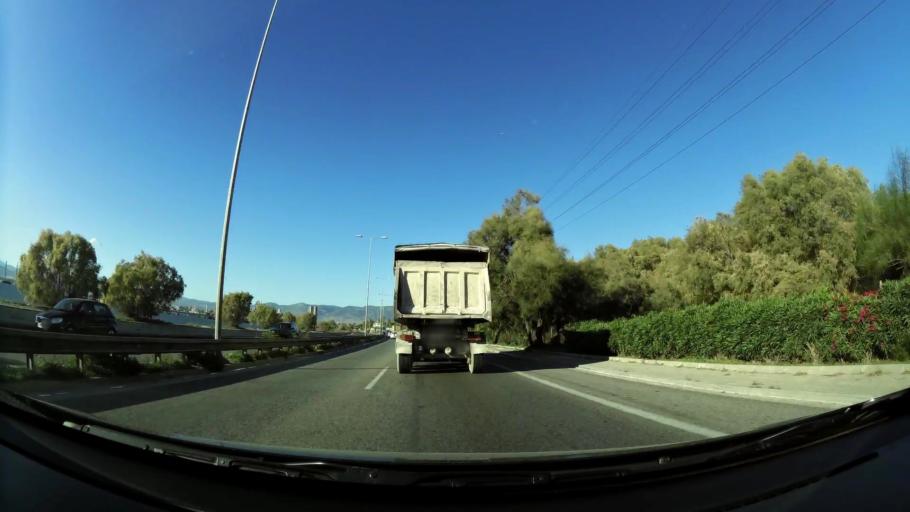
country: GR
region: Attica
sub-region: Nomarchia Athinas
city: Skaramangas
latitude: 38.0217
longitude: 23.5992
